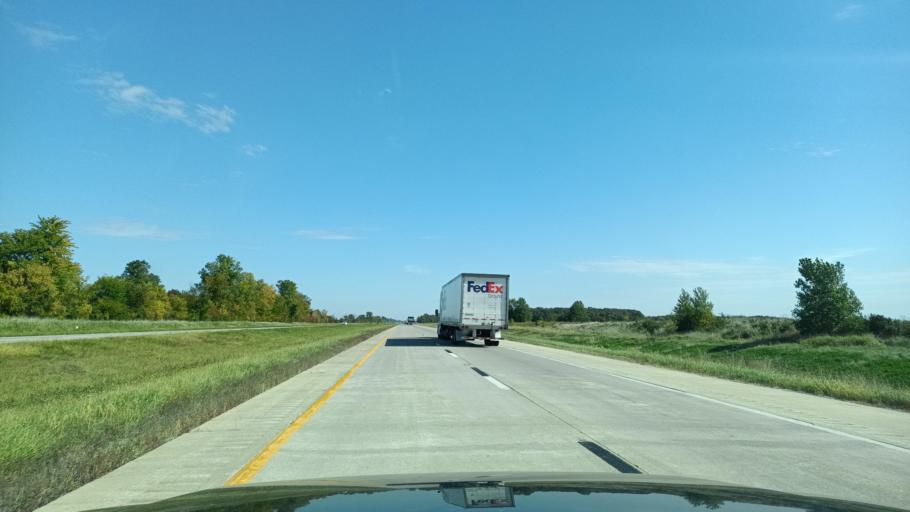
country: US
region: Ohio
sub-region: Paulding County
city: Antwerp
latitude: 41.1975
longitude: -84.6749
